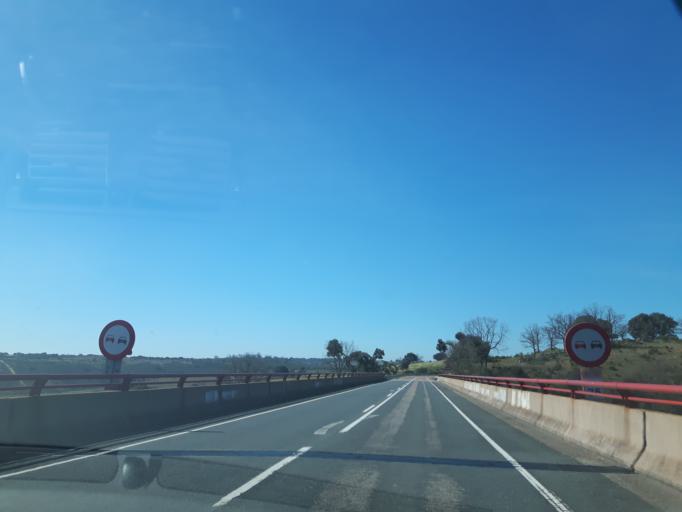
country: ES
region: Castille and Leon
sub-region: Provincia de Salamanca
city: Cerralbo
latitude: 40.9850
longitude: -6.5599
